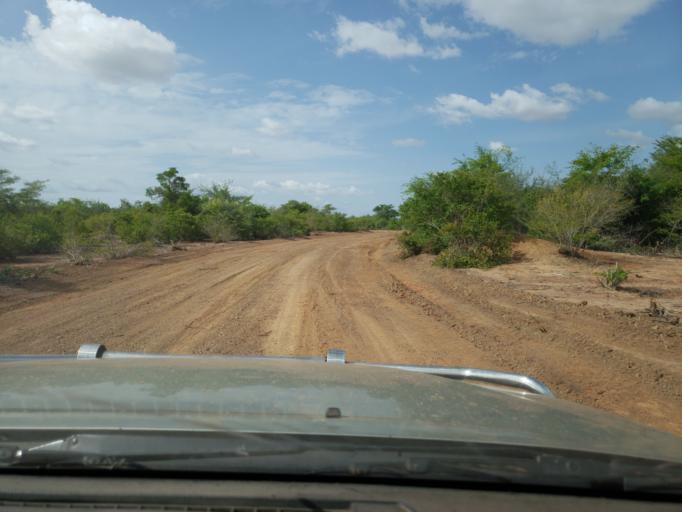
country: ML
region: Segou
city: Bla
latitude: 12.7778
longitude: -5.6098
